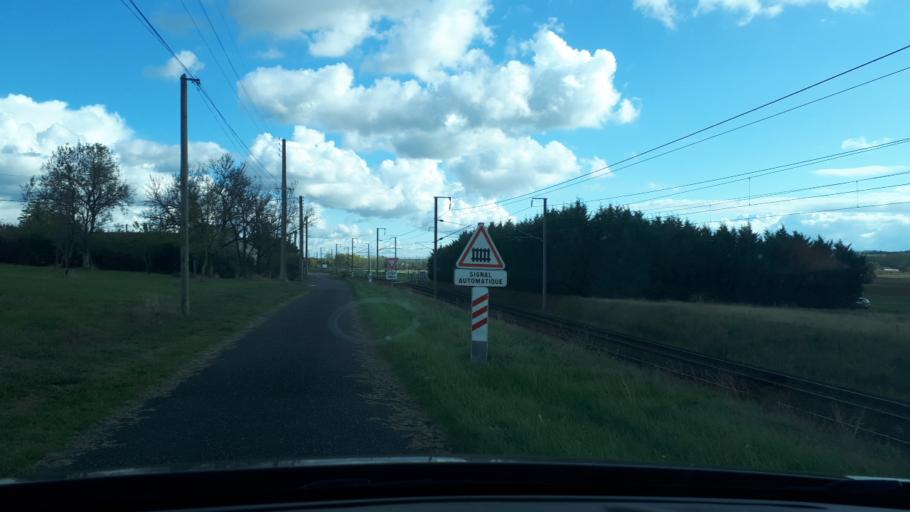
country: FR
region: Centre
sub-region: Departement du Loir-et-Cher
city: Mareuil-sur-Cher
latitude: 47.3017
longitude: 1.3529
